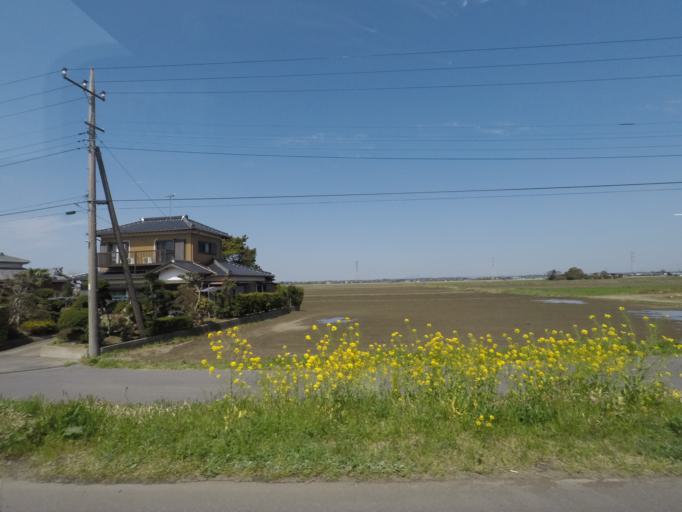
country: JP
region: Ibaraki
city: Edosaki
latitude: 35.8720
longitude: 140.3282
